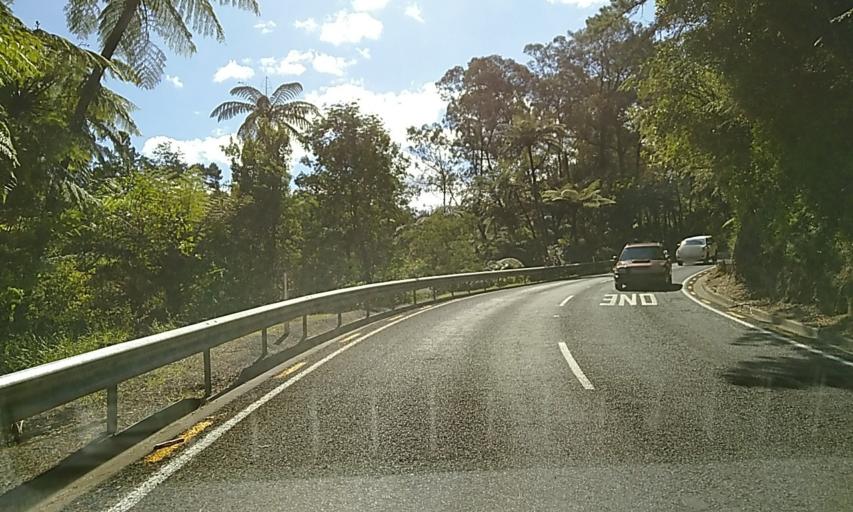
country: NZ
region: Bay of Plenty
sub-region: Tauranga City
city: Tauranga
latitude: -37.8055
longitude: 176.0434
